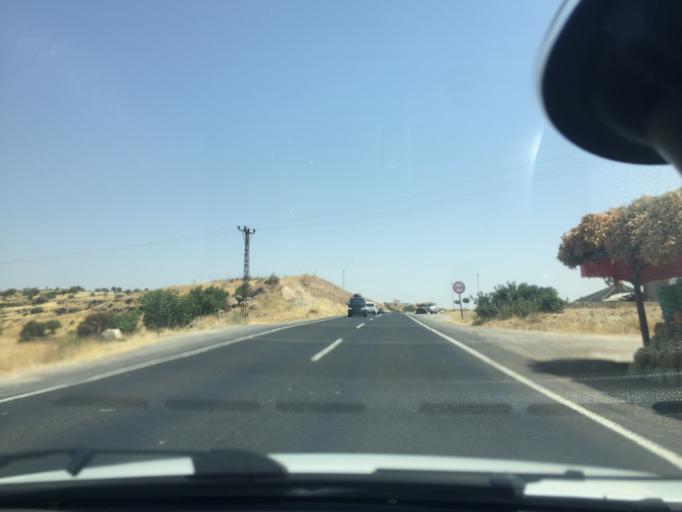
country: TR
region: Mardin
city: Acirli
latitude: 37.4473
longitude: 41.2771
